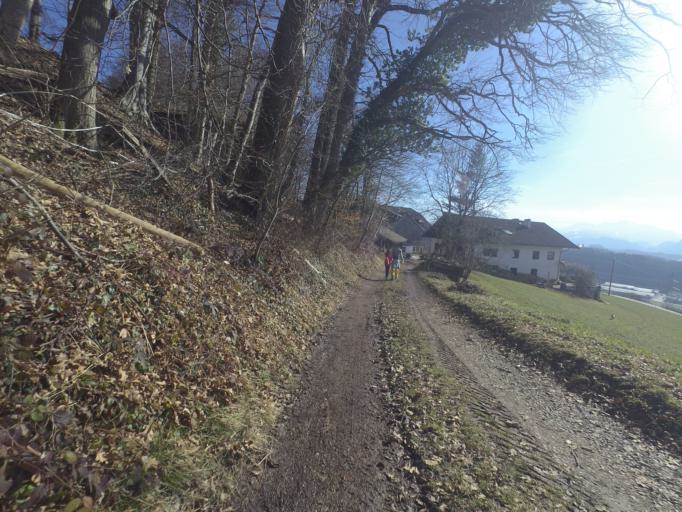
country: AT
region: Salzburg
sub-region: Politischer Bezirk Salzburg-Umgebung
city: Bergheim
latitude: 47.8530
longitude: 13.0361
